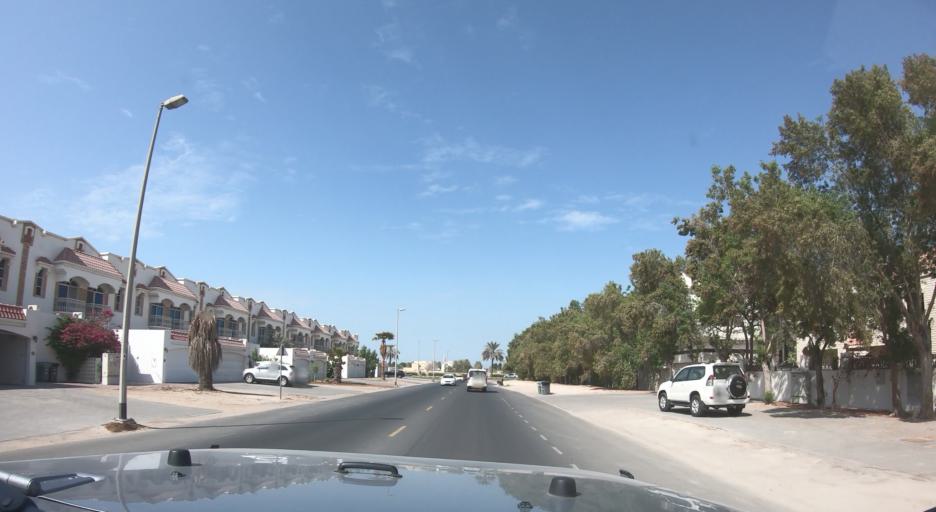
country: AE
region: Dubai
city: Dubai
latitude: 25.1614
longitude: 55.2230
